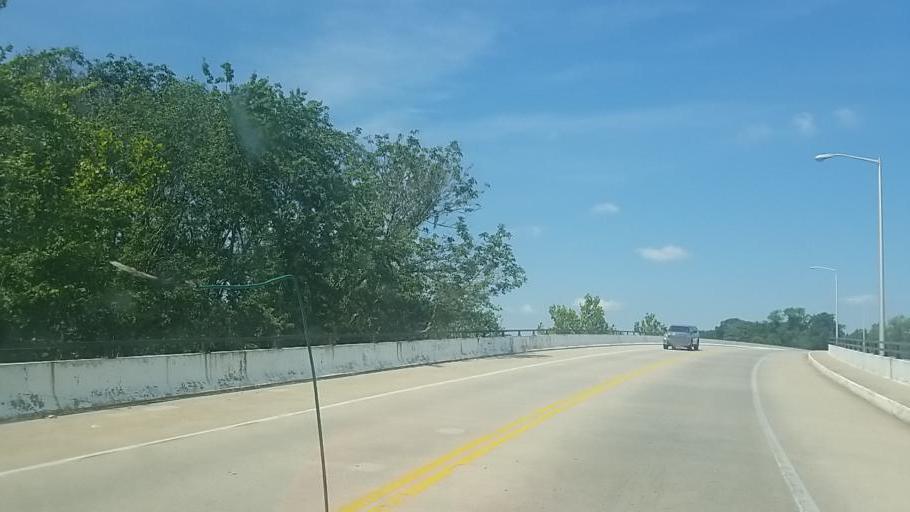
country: US
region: Maryland
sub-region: Caroline County
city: Denton
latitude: 38.8877
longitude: -75.8372
